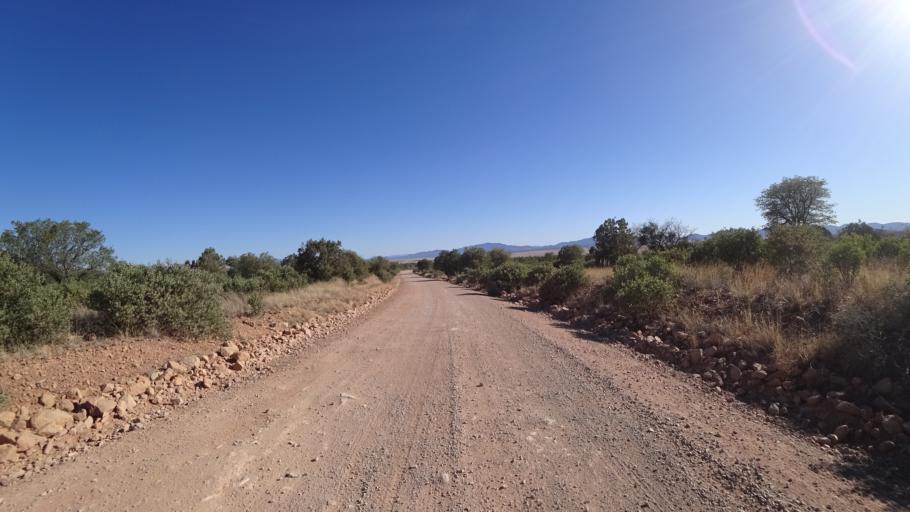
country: US
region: Arizona
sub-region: Cochise County
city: Sierra Vista
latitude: 31.4935
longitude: -110.5554
